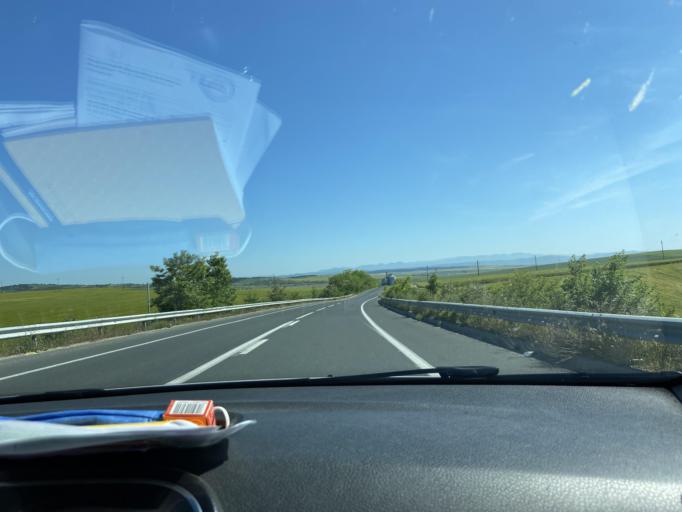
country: MK
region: Veles
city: Veles
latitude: 41.7581
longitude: 21.8288
